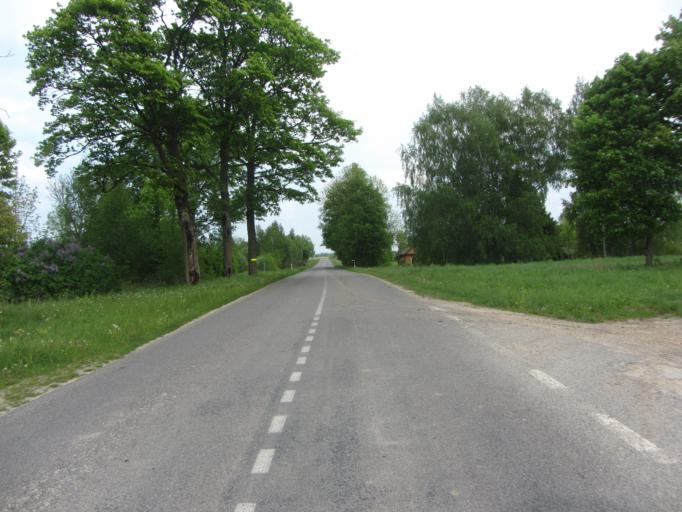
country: LT
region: Utenos apskritis
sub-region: Anyksciai
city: Anyksciai
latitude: 55.5730
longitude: 25.2992
